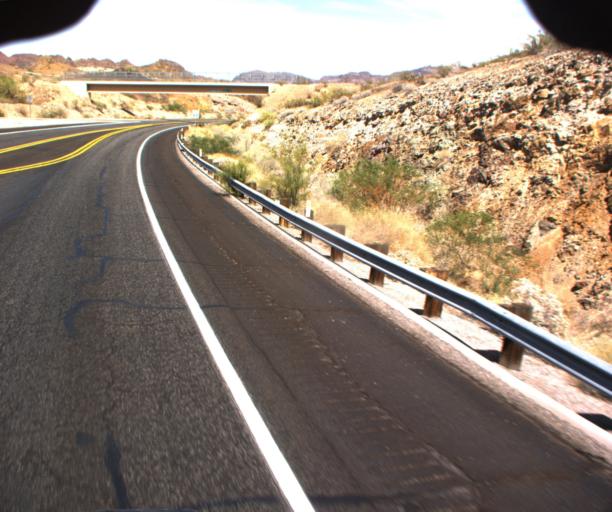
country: US
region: Arizona
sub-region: La Paz County
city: Cienega Springs
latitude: 34.2542
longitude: -114.1609
